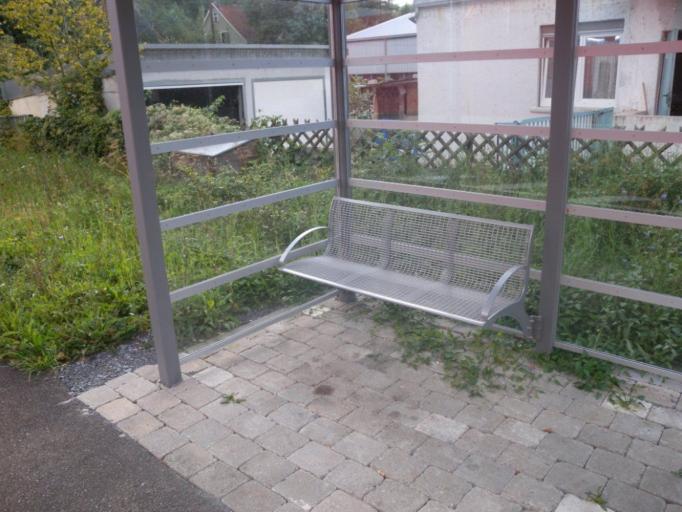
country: DE
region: Baden-Wuerttemberg
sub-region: Regierungsbezirk Stuttgart
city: Nordheim
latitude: 49.1090
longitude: 9.1486
